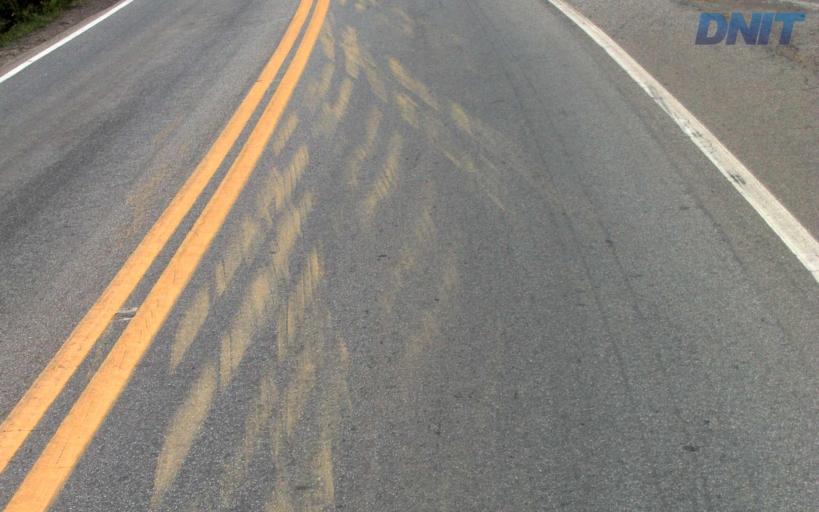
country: BR
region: Minas Gerais
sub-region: Ipaba
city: Ipaba
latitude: -19.4033
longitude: -42.4837
